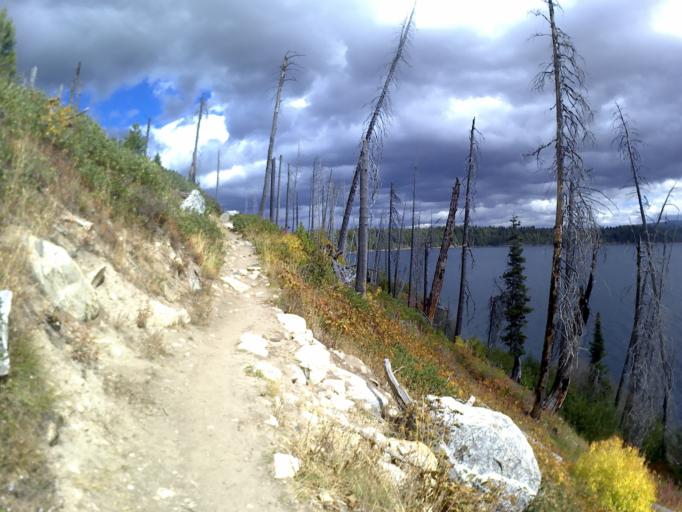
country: US
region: Wyoming
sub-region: Teton County
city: Moose Wilson Road
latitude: 43.7752
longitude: -110.7358
